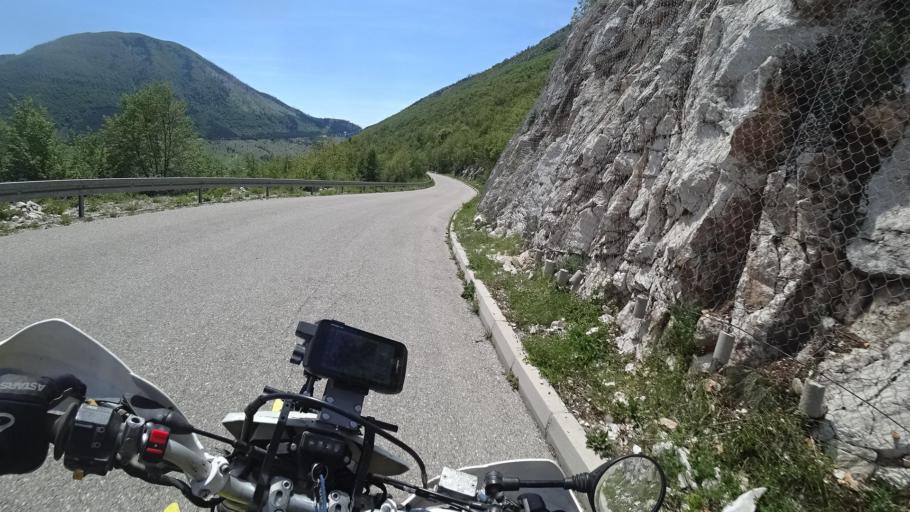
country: BA
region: Federation of Bosnia and Herzegovina
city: Potoci
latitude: 43.4799
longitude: 17.9934
